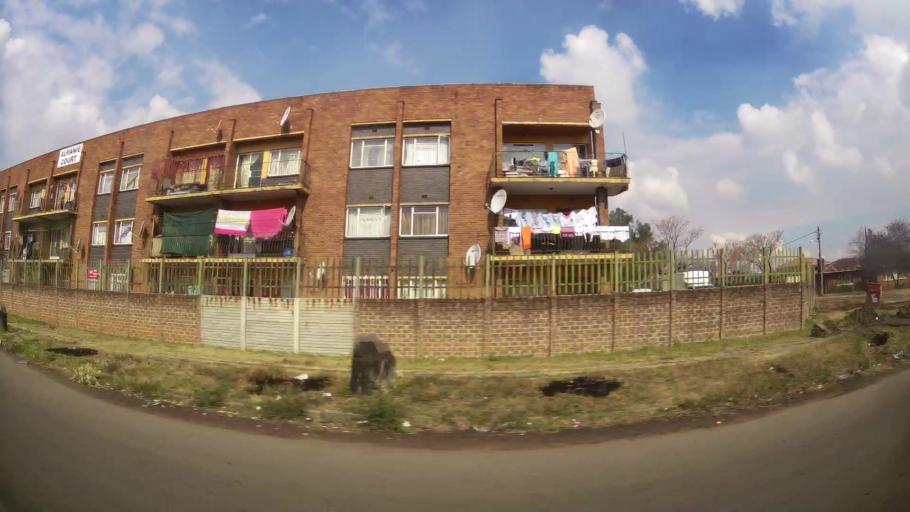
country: ZA
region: Gauteng
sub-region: Sedibeng District Municipality
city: Vereeniging
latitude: -26.6838
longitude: 27.9252
